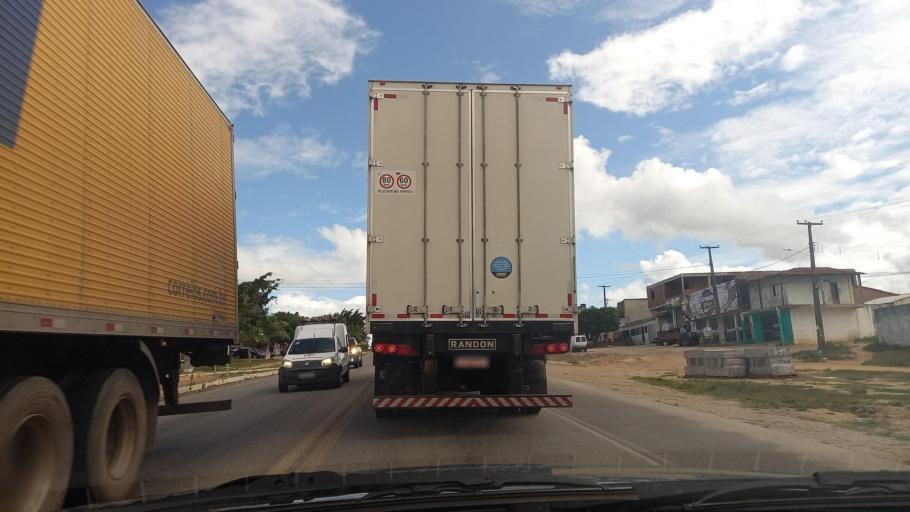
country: BR
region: Pernambuco
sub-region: Lajedo
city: Lajedo
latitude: -8.7113
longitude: -36.4199
